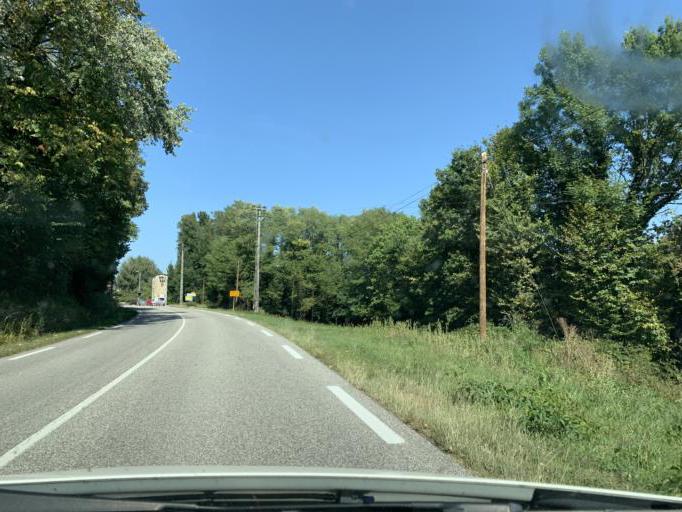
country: FR
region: Rhone-Alpes
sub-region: Departement de la Savoie
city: Yenne
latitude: 45.6726
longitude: 5.6797
